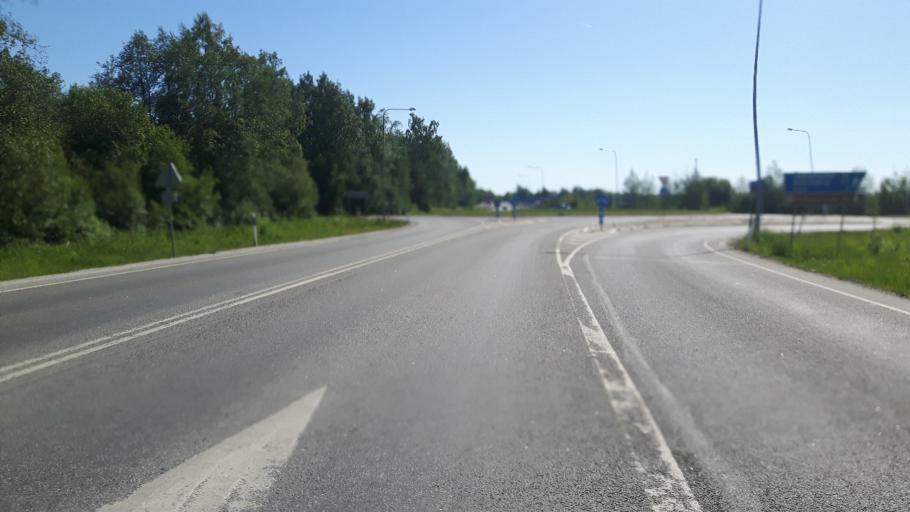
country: EE
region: Raplamaa
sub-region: Rapla vald
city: Rapla
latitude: 59.0149
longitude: 24.8019
